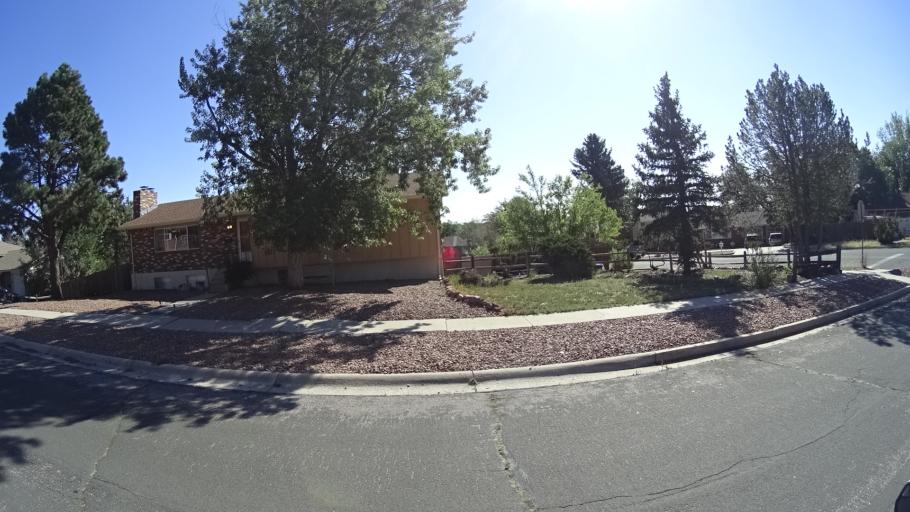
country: US
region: Colorado
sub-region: El Paso County
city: Cimarron Hills
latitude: 38.8657
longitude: -104.7619
